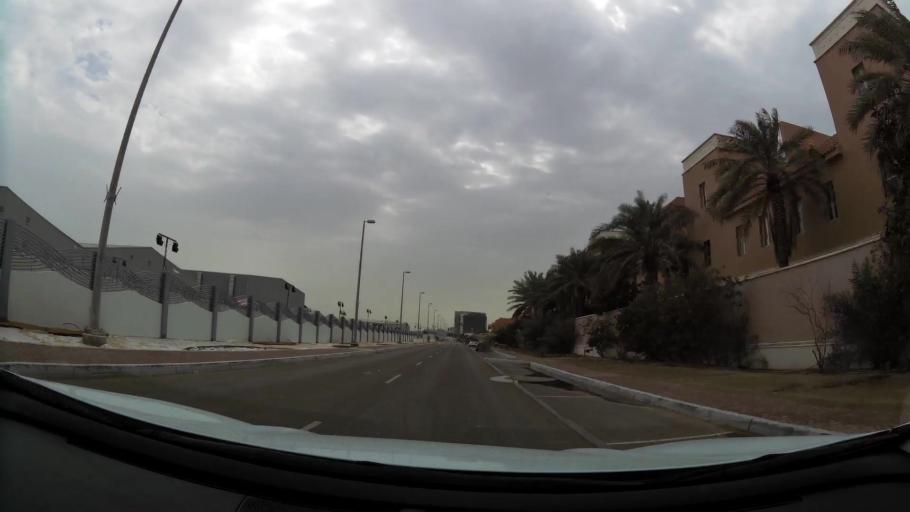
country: AE
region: Abu Dhabi
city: Abu Dhabi
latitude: 24.4291
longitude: 54.4491
